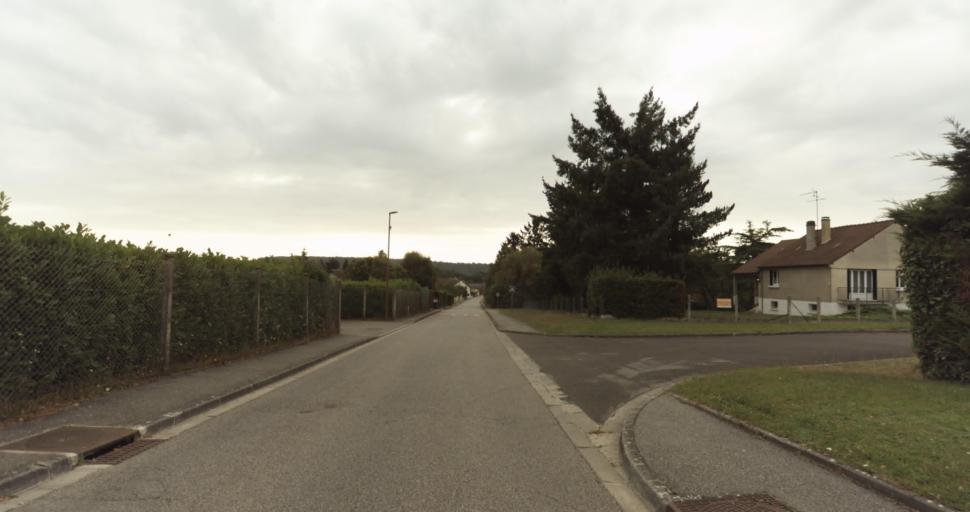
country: FR
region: Haute-Normandie
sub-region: Departement de l'Eure
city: Marcilly-sur-Eure
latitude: 48.8251
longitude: 1.3388
